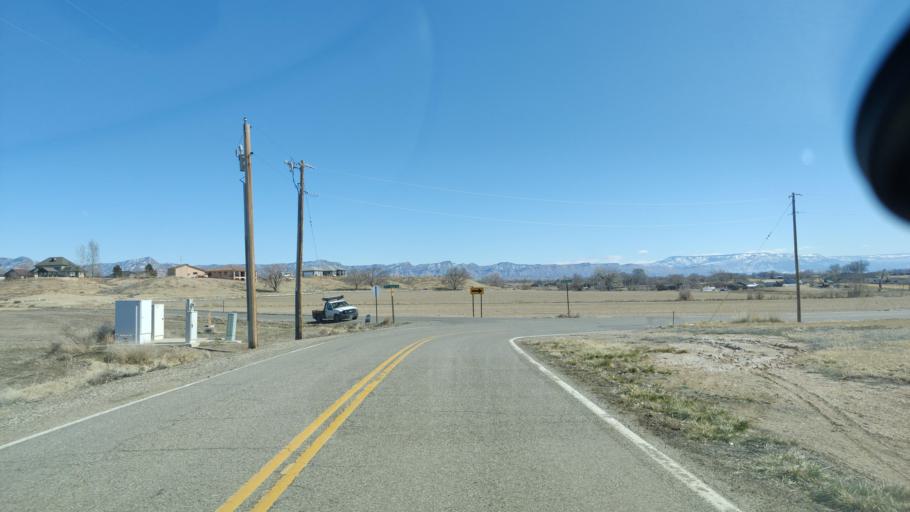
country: US
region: Colorado
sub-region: Mesa County
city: Fruita
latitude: 39.2040
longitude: -108.7112
